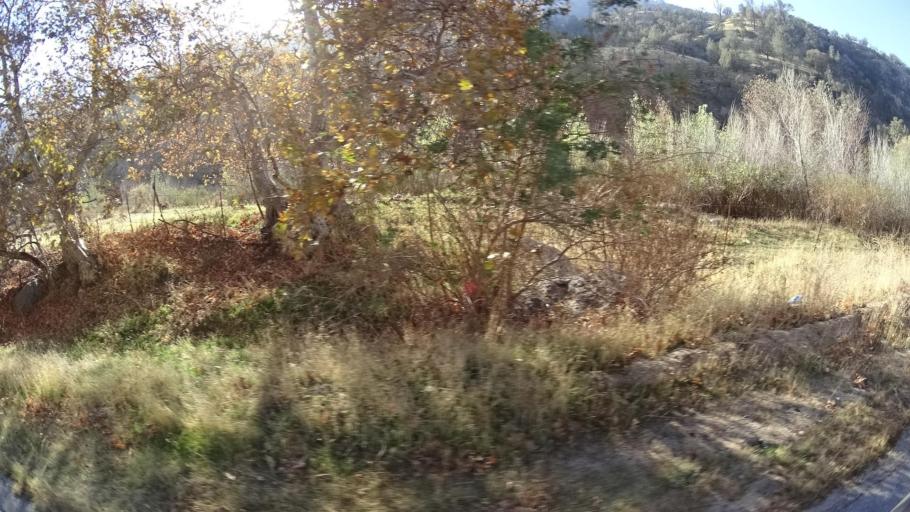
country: US
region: California
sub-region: Kern County
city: Bear Valley Springs
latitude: 35.3120
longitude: -118.5638
